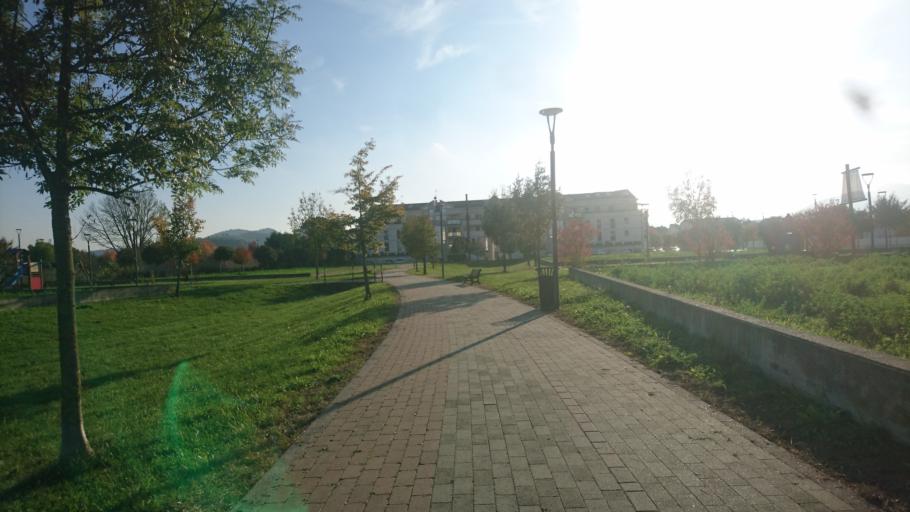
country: IT
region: Veneto
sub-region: Provincia di Padova
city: Montegrotto Terme
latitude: 45.3445
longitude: 11.7800
